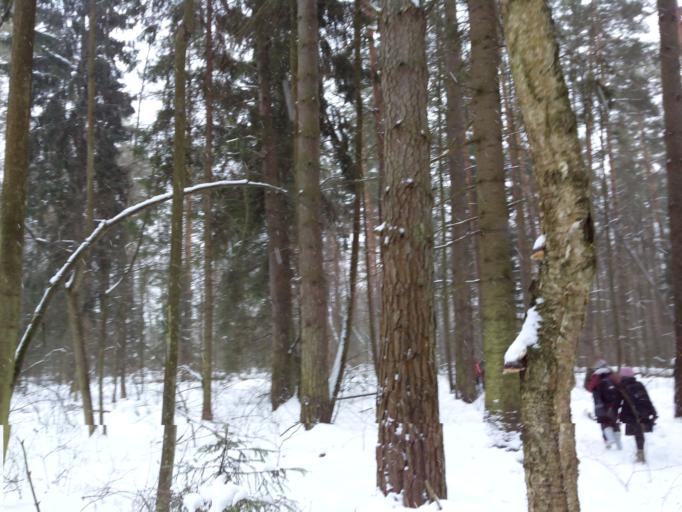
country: RU
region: Moskovskaya
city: Bol'shiye Vyazemy
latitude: 55.6641
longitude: 36.9883
